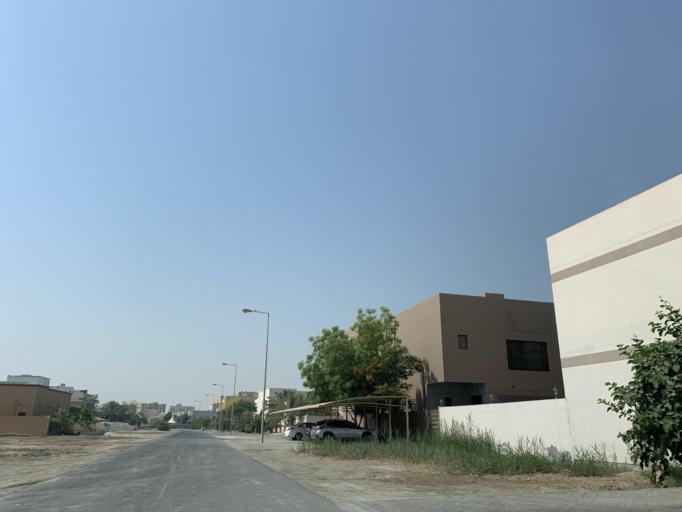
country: BH
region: Manama
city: Jidd Hafs
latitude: 26.1983
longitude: 50.5129
